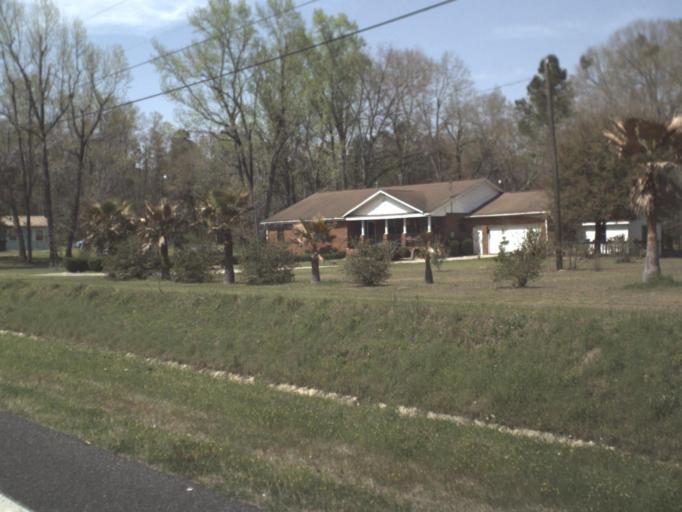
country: US
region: Florida
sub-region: Gadsden County
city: Quincy
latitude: 30.5549
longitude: -84.5260
